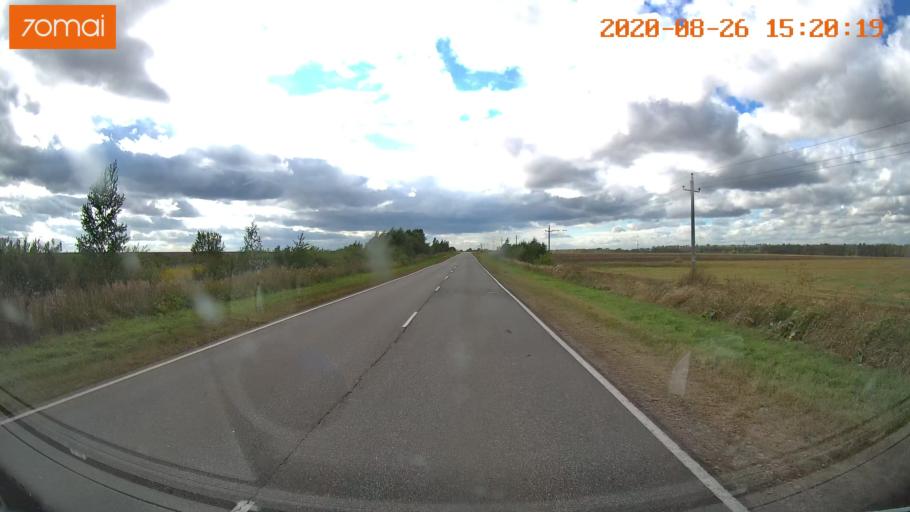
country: RU
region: Tula
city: Severo-Zadonsk
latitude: 54.1426
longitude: 38.4994
